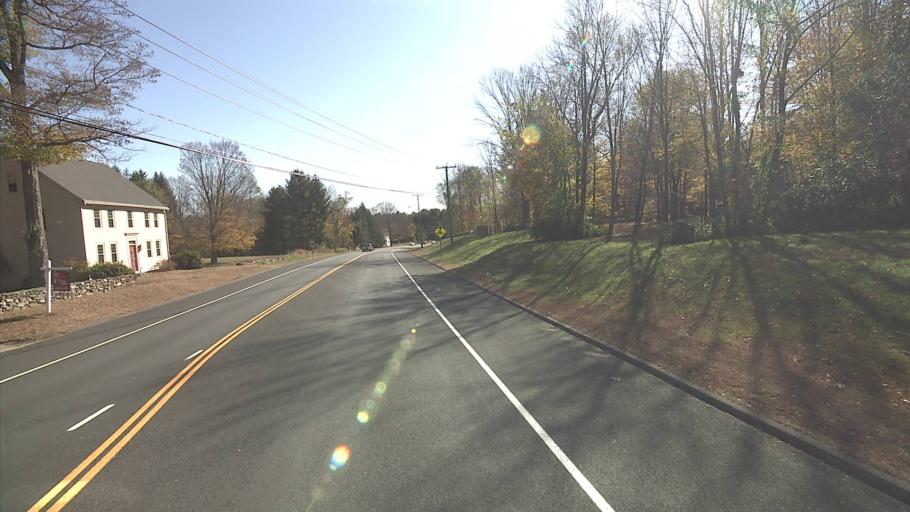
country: US
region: Connecticut
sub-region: Tolland County
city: Coventry Lake
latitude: 41.7466
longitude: -72.3885
